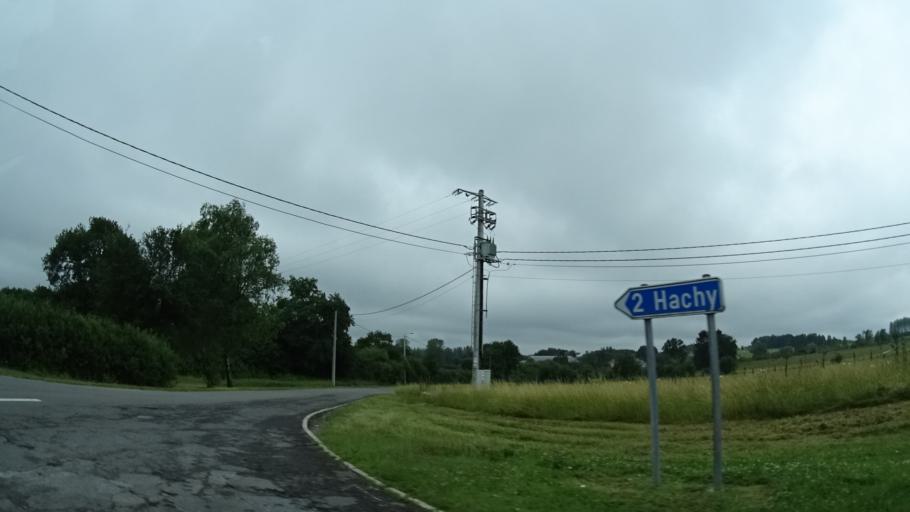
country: BE
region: Wallonia
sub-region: Province du Luxembourg
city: Habay-la-Vieille
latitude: 49.7147
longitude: 5.6884
